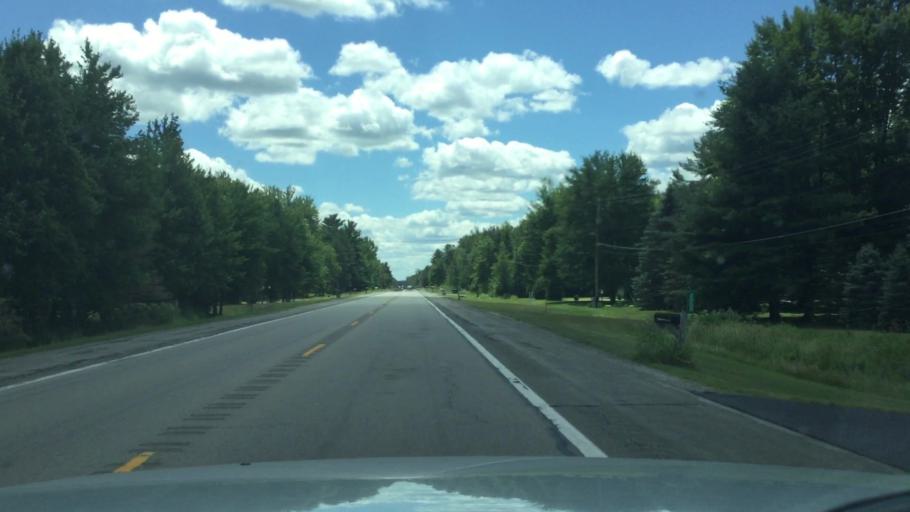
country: US
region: Michigan
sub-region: Saginaw County
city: Shields
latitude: 43.3945
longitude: -84.1312
